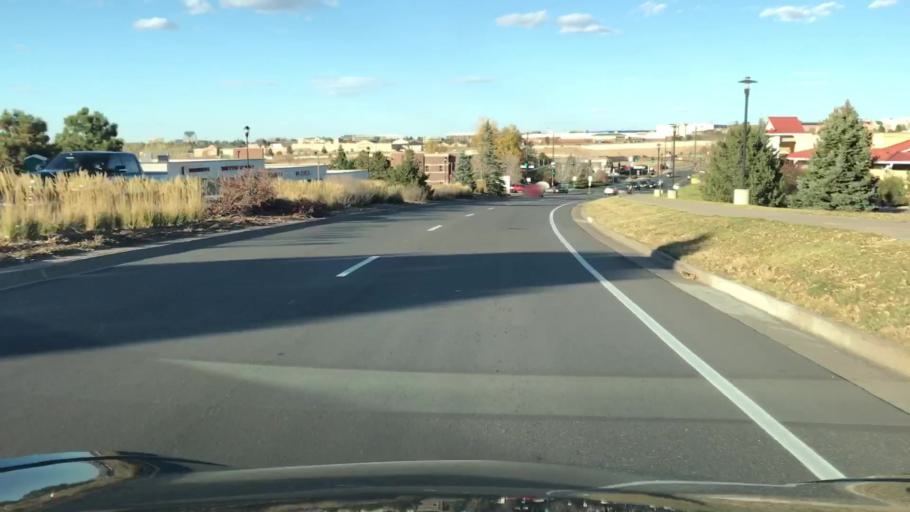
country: US
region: Colorado
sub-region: Adams County
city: Lone Tree
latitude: 39.5532
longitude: -104.8853
